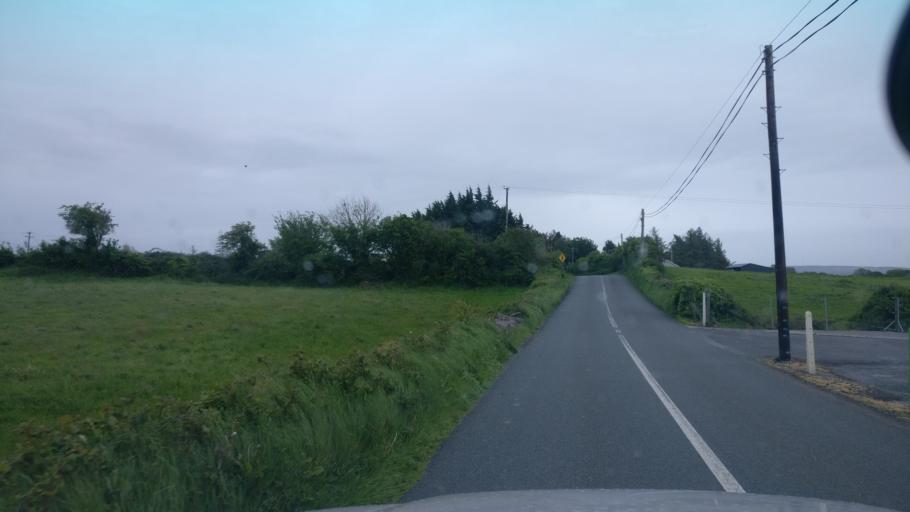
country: IE
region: Connaught
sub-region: County Galway
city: Gort
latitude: 53.0687
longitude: -8.7820
